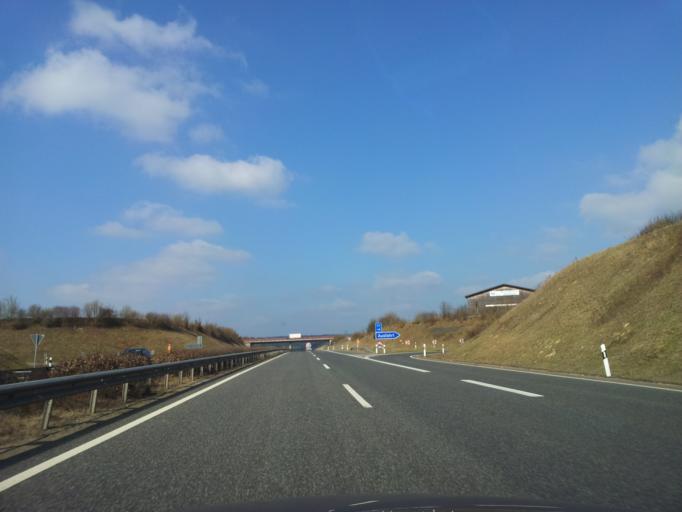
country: DE
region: Rheinland-Pfalz
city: Landscheid
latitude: 49.9904
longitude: 6.7828
